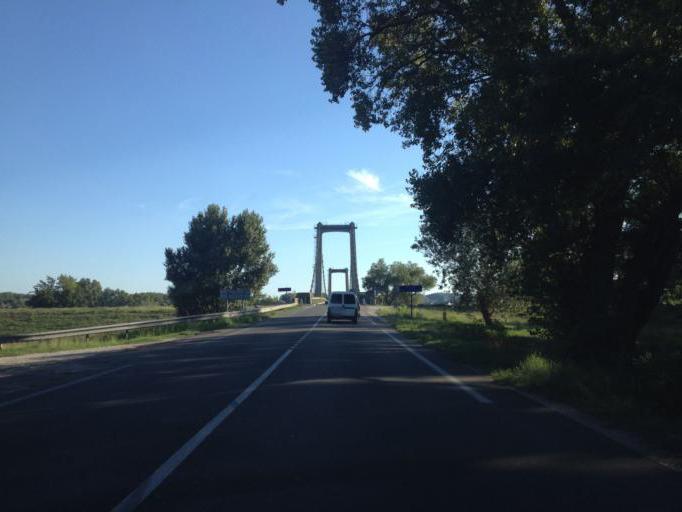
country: FR
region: Languedoc-Roussillon
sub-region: Departement du Gard
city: Montfaucon
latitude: 44.0742
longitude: 4.7703
